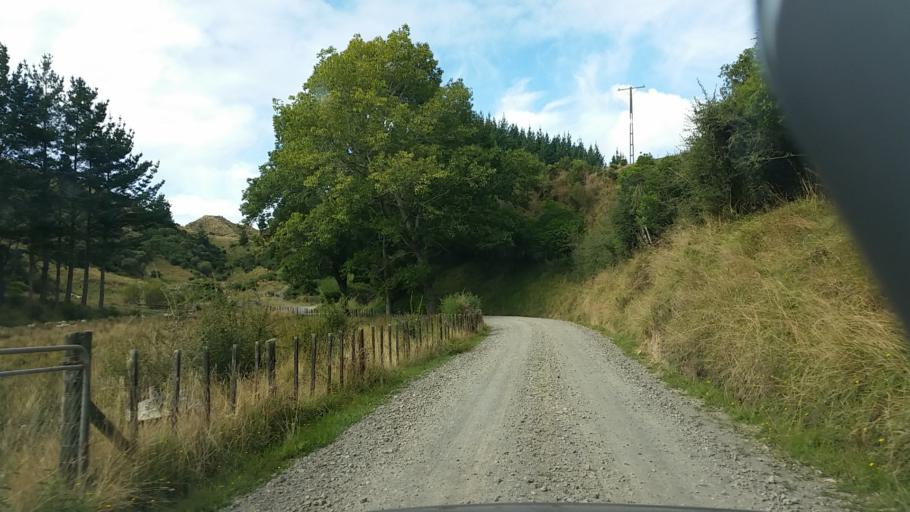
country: NZ
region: Taranaki
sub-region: South Taranaki District
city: Eltham
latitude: -39.2315
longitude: 174.4741
